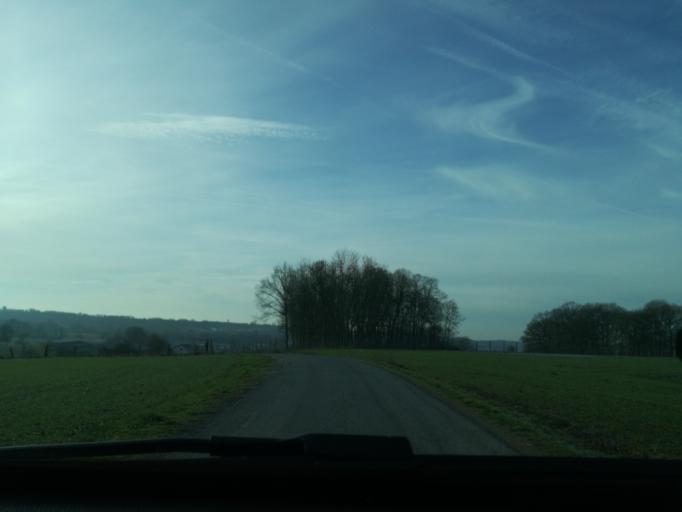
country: FR
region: Lorraine
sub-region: Departement de la Meuse
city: Revigny-sur-Ornain
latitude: 48.8277
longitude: 5.0586
